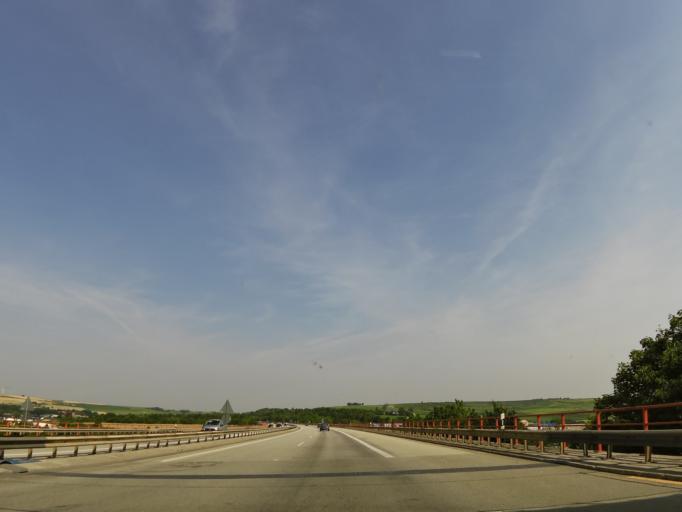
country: DE
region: Rheinland-Pfalz
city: Alzey
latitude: 49.7465
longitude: 8.1348
